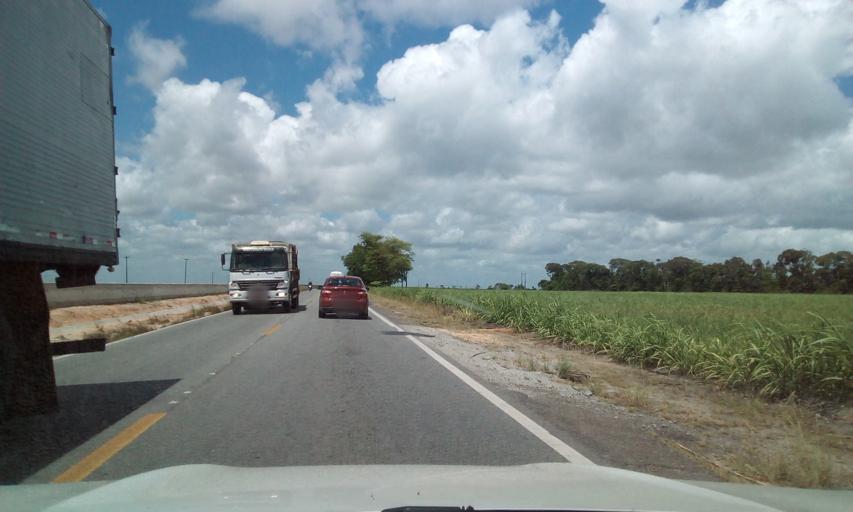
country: BR
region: Alagoas
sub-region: Pilar
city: Pilar
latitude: -9.6111
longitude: -36.0276
